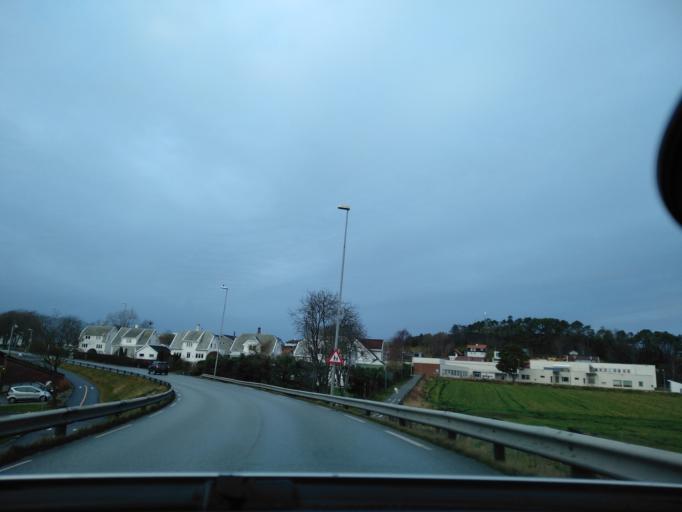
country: NO
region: Rogaland
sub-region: Randaberg
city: Randaberg
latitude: 58.9982
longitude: 5.6252
